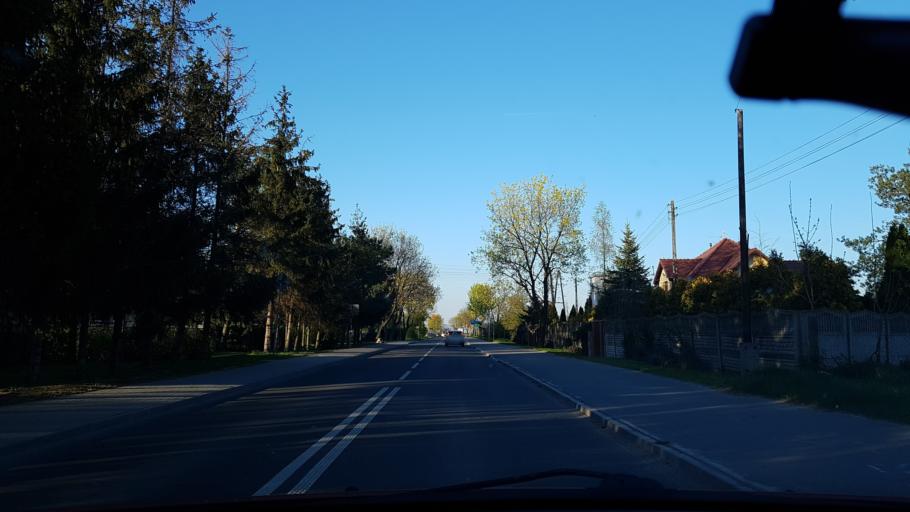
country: PL
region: Opole Voivodeship
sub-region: Powiat nyski
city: Nysa
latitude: 50.4375
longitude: 17.3084
